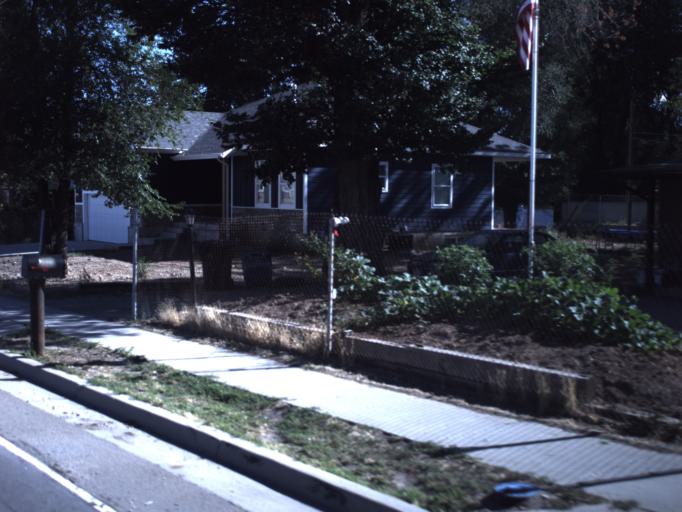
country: US
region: Utah
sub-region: Salt Lake County
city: Magna
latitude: 40.7091
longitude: -112.0918
